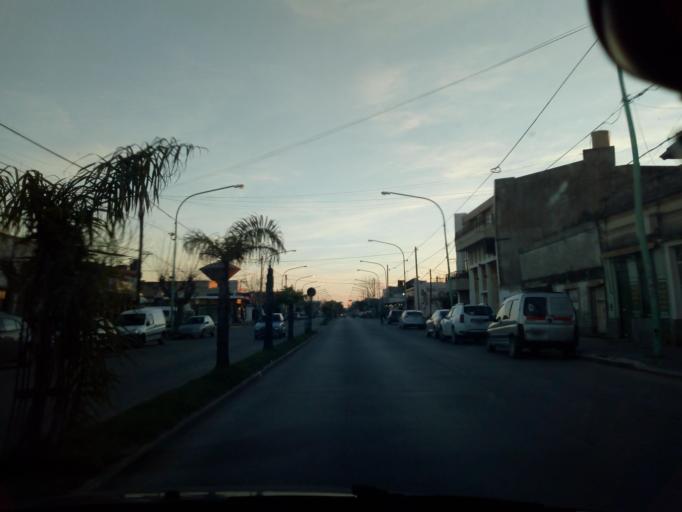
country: AR
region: Buenos Aires
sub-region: Partido de Ensenada
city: Ensenada
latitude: -34.8662
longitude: -57.9064
